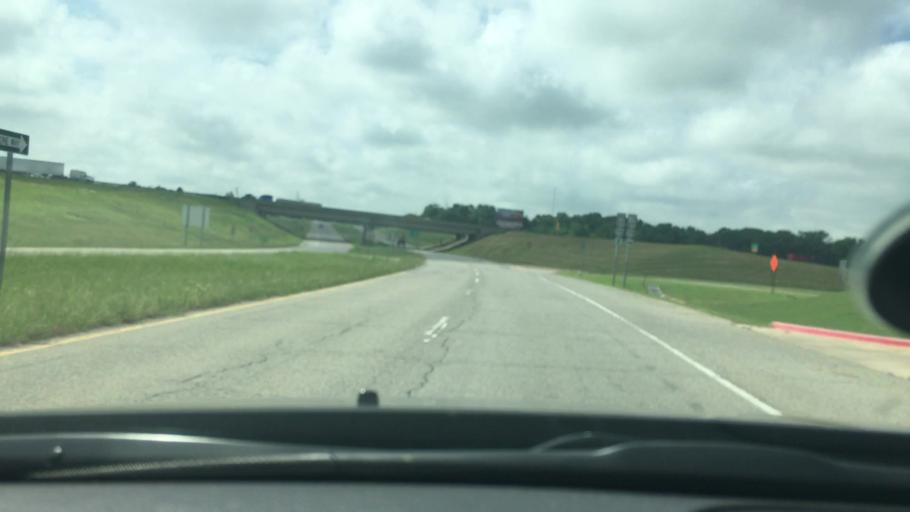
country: US
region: Oklahoma
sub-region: Bryan County
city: Durant
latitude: 34.0398
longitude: -96.3760
